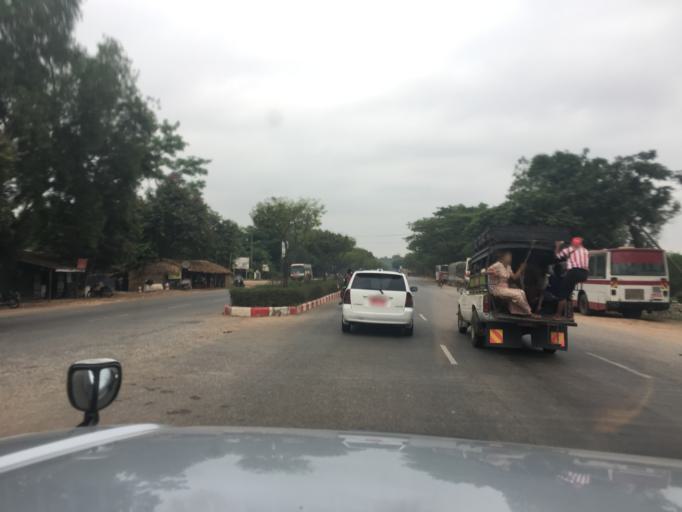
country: MM
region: Bago
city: Thanatpin
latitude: 17.1864
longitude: 96.3880
